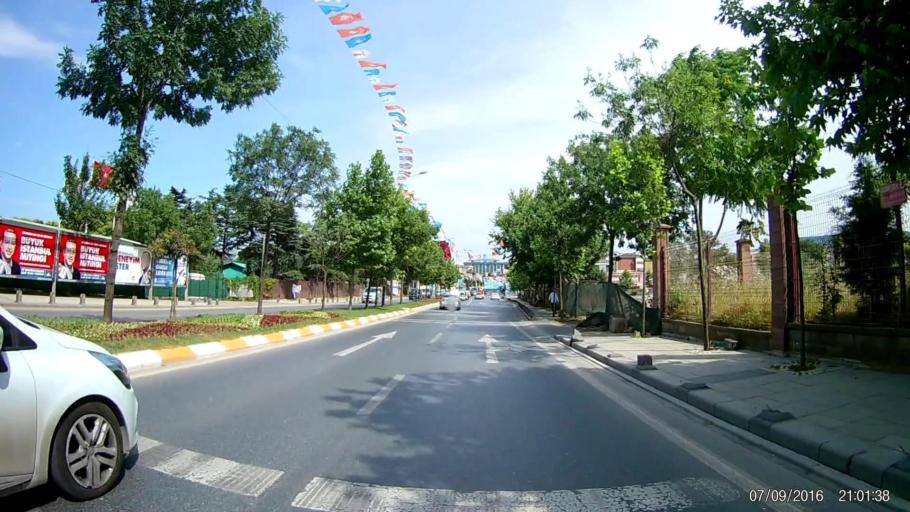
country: TR
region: Istanbul
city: Sultanbeyli
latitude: 40.9732
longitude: 29.2464
